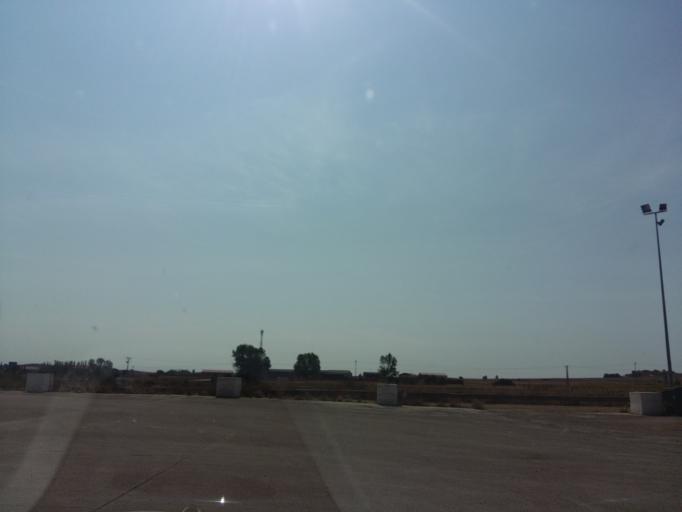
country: ES
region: Castille and Leon
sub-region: Provincia de Palencia
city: Villaherreros
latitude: 42.3912
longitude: -4.4743
